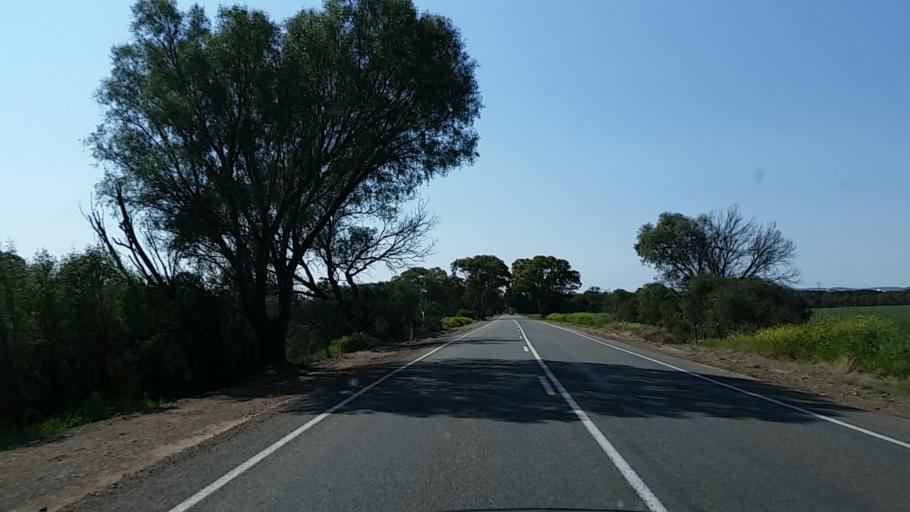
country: AU
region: South Australia
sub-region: Port Pirie City and Dists
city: Crystal Brook
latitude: -33.2641
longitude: 138.3350
